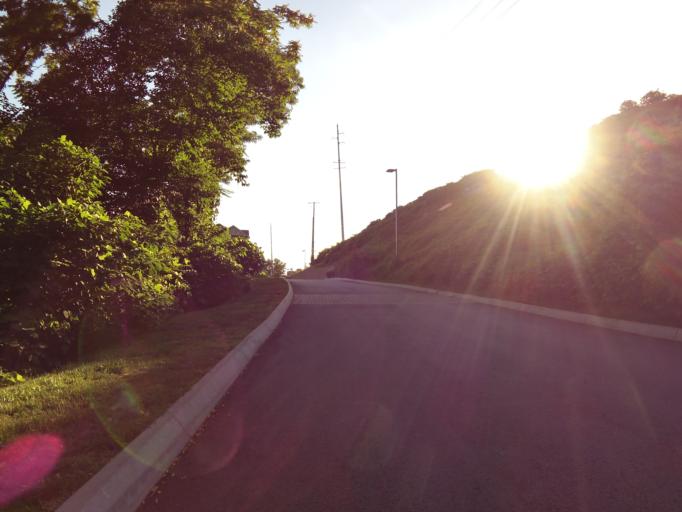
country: US
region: Tennessee
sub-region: Knox County
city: Knoxville
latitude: 35.9638
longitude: -83.9073
